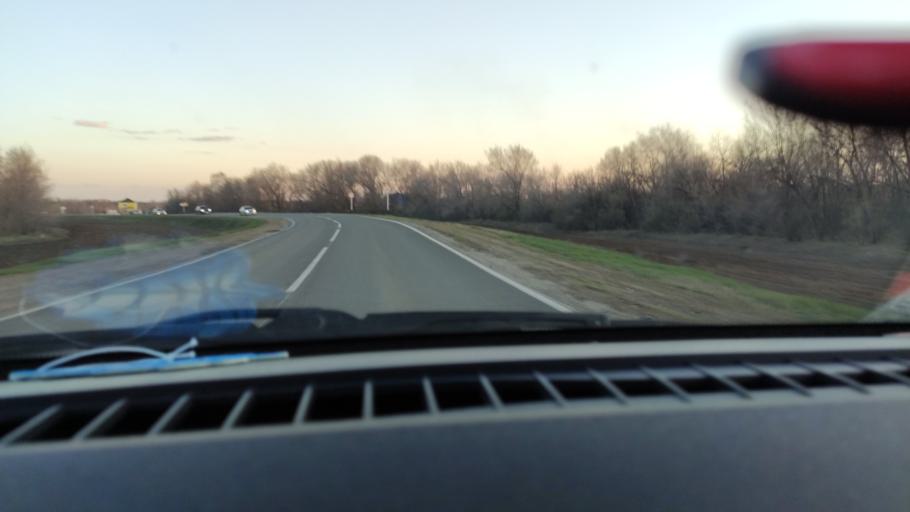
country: RU
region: Saratov
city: Privolzhskiy
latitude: 51.3516
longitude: 46.0449
